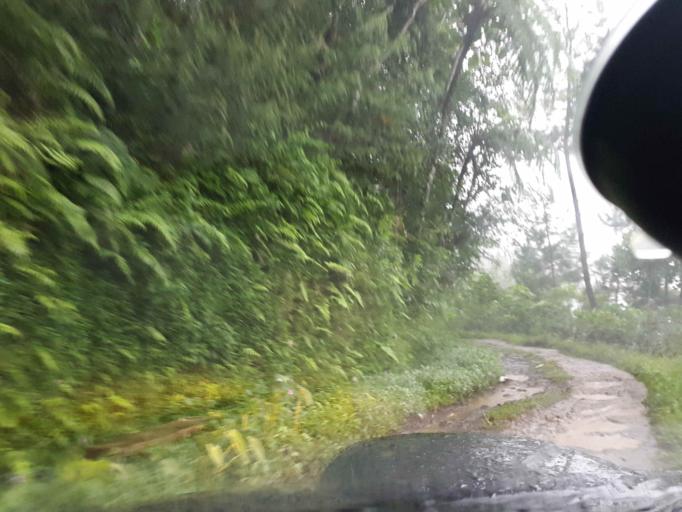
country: ID
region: Central Java
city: Wonosobo
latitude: -7.5218
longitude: 109.8758
